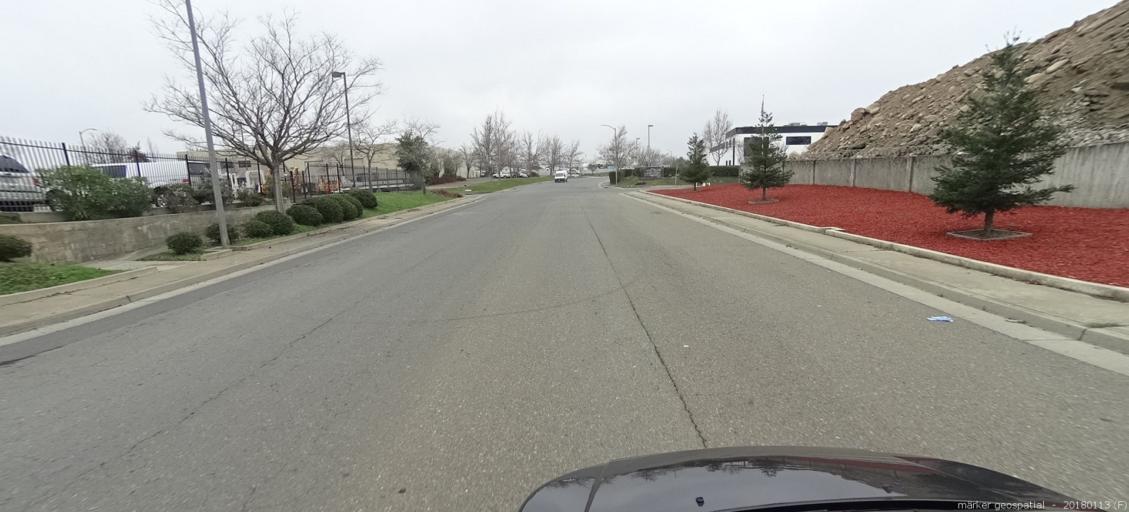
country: US
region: California
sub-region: Sacramento County
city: Gold River
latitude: 38.5798
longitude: -121.2552
